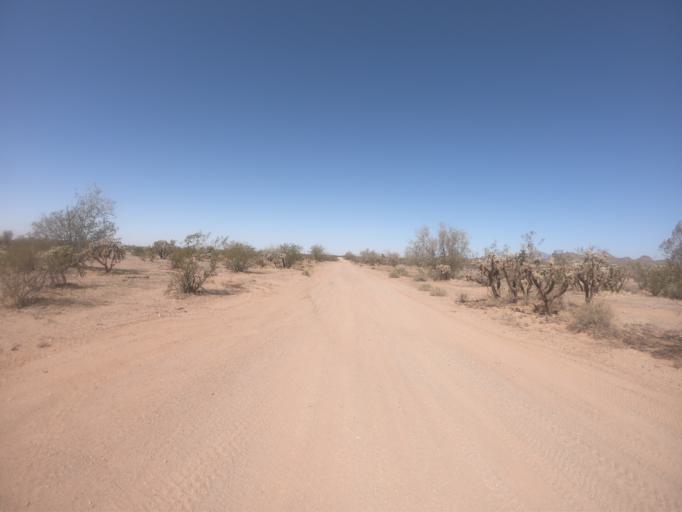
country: US
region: Arizona
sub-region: Pinal County
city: Gold Camp
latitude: 33.2420
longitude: -111.3179
